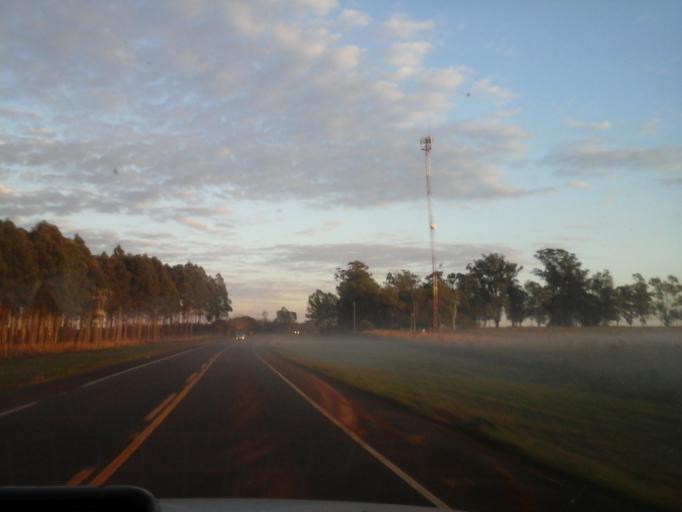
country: PY
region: Itapua
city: General Delgado
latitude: -27.0602
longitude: -56.6288
